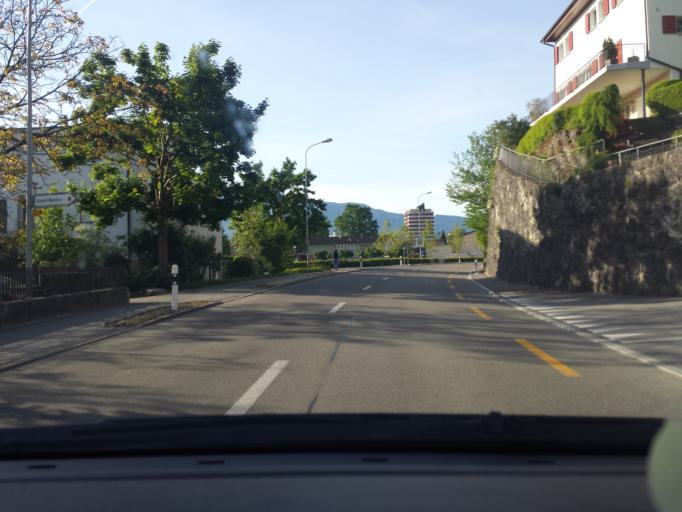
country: CH
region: Appenzell Innerrhoden
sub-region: Appenzell Inner Rhodes
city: Balgach
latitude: 47.4154
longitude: 9.6246
